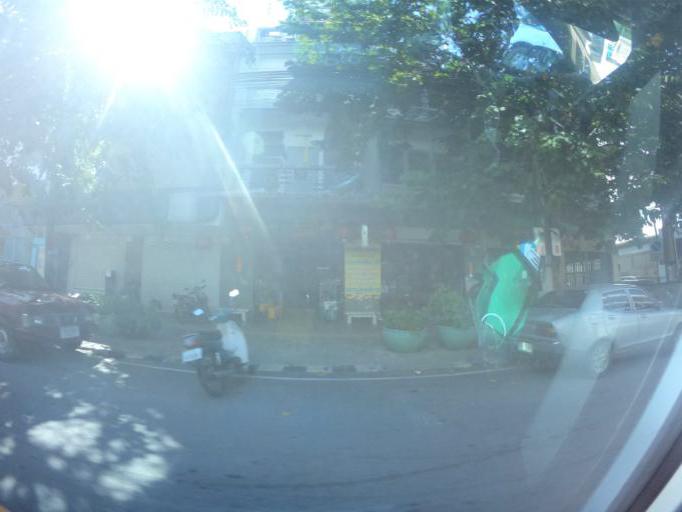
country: TH
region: Khon Kaen
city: Khon Kaen
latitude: 16.4807
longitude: 102.9609
